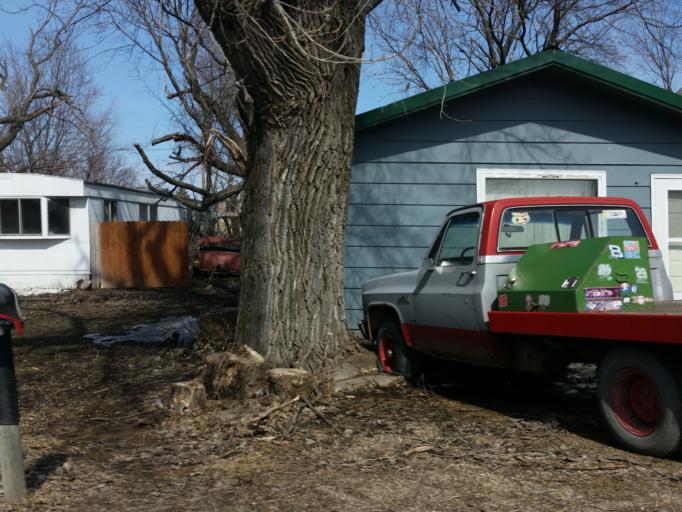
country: US
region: North Dakota
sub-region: Walsh County
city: Grafton
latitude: 48.2954
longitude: -97.2559
